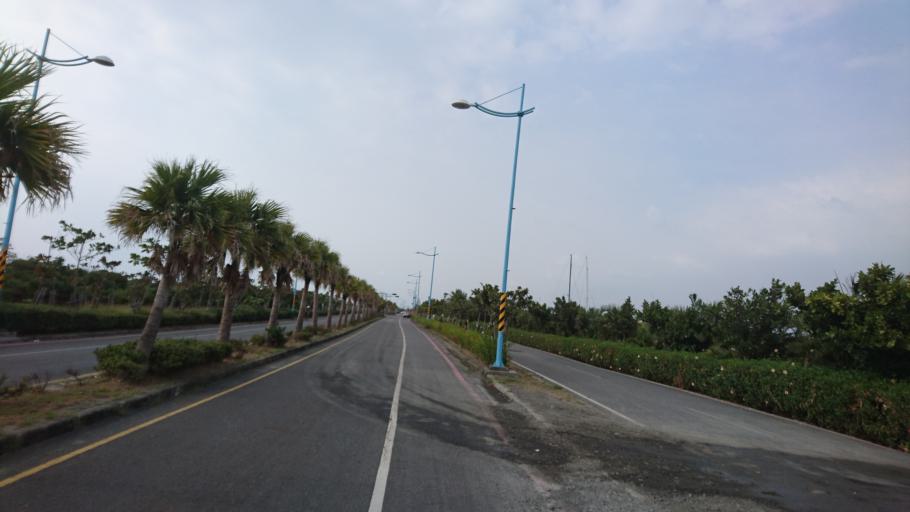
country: TW
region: Taiwan
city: Fengshan
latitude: 22.4356
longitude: 120.4785
